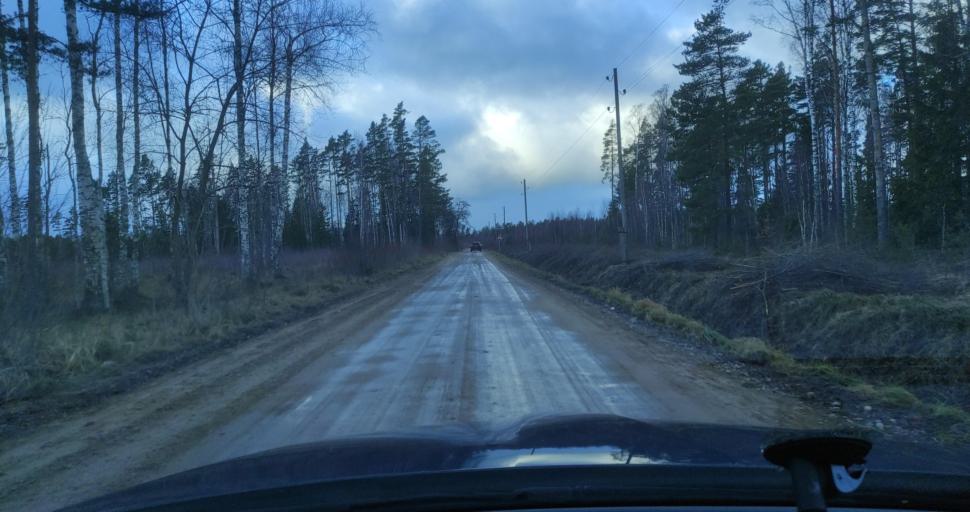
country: LV
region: Pavilostas
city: Pavilosta
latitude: 56.8579
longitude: 21.1711
